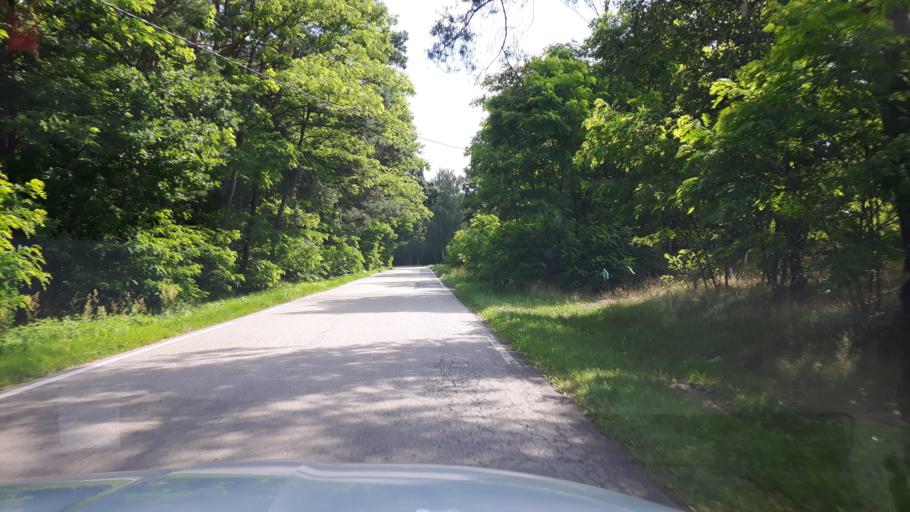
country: PL
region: Masovian Voivodeship
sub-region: Powiat wolominski
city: Strachowka
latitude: 52.4436
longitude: 21.5760
